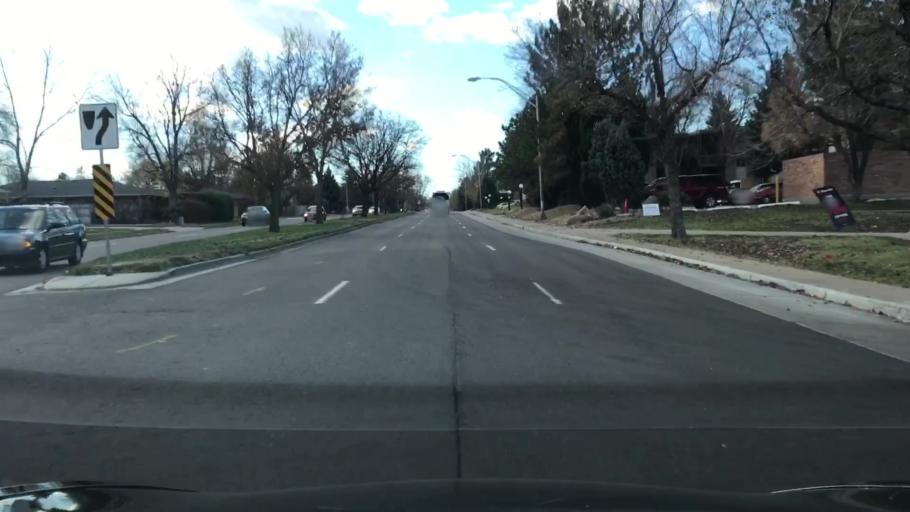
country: US
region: Colorado
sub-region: Arapahoe County
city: Glendale
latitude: 39.6662
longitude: -104.9131
